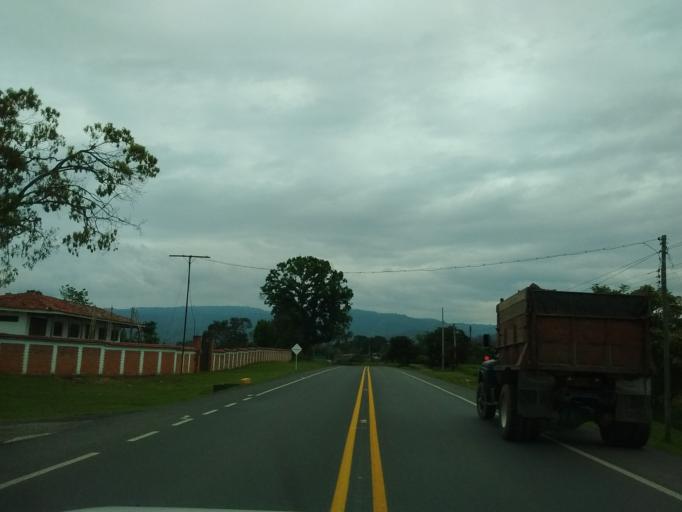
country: CO
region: Cauca
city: Cajibio
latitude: 2.5870
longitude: -76.5352
